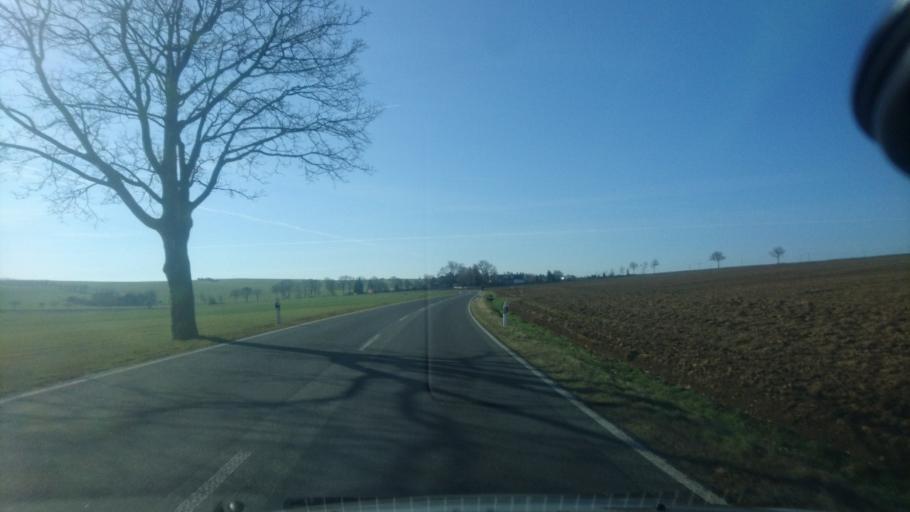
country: DE
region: Saxony
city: Neuensalz
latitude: 50.4922
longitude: 12.2202
